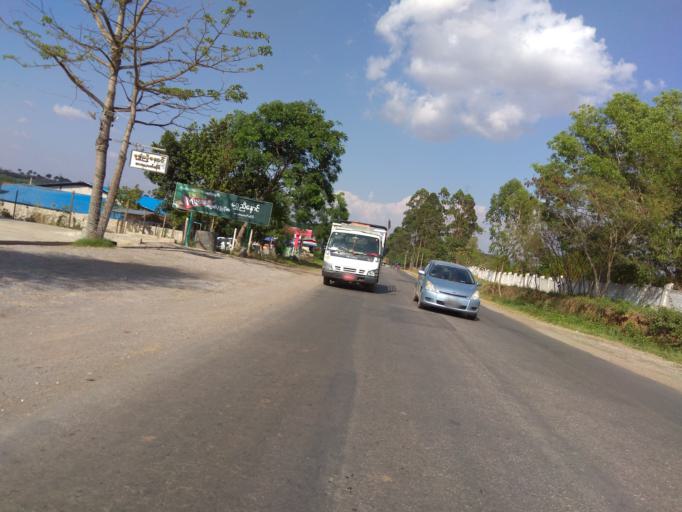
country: MM
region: Shan
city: Taunggyi
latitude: 20.6701
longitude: 96.6612
